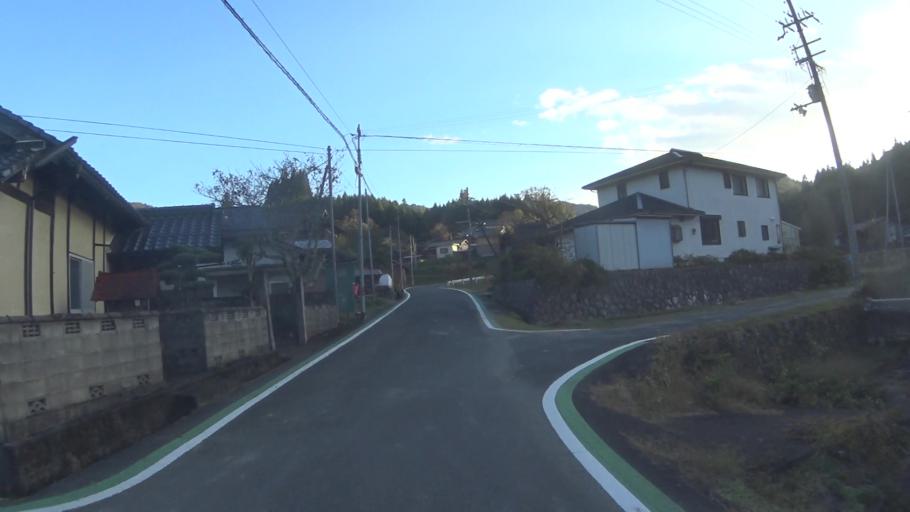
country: JP
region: Kyoto
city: Ayabe
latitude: 35.2809
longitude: 135.2505
